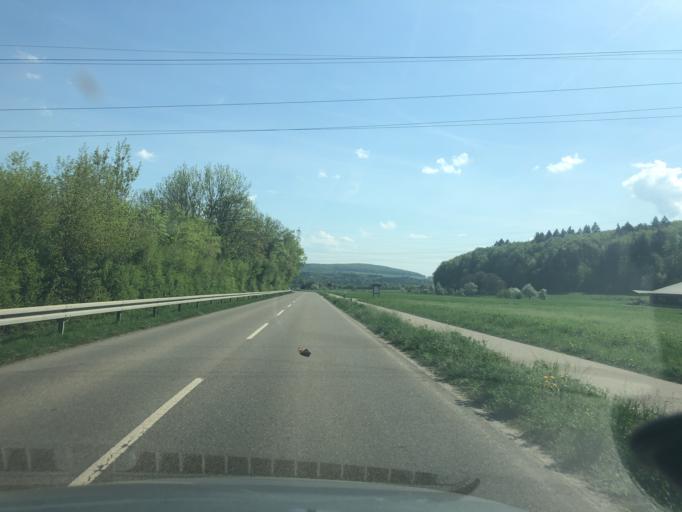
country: CH
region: Aargau
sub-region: Bezirk Zurzach
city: Koblenz
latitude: 47.6381
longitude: 8.2484
